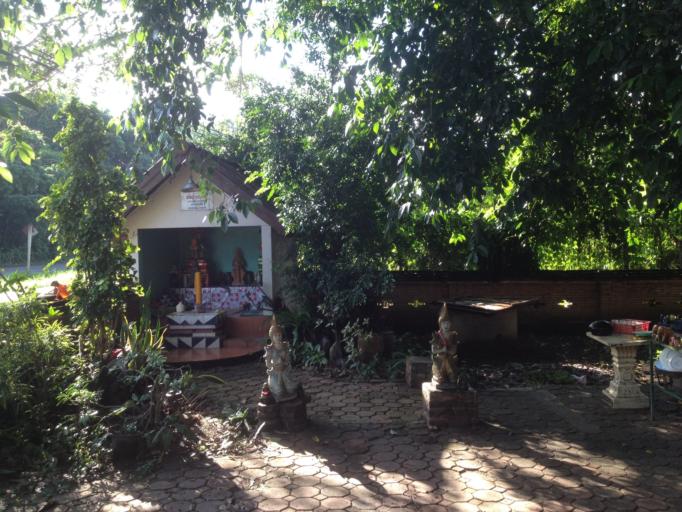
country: TH
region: Chiang Mai
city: Hang Dong
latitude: 18.7029
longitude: 98.9155
